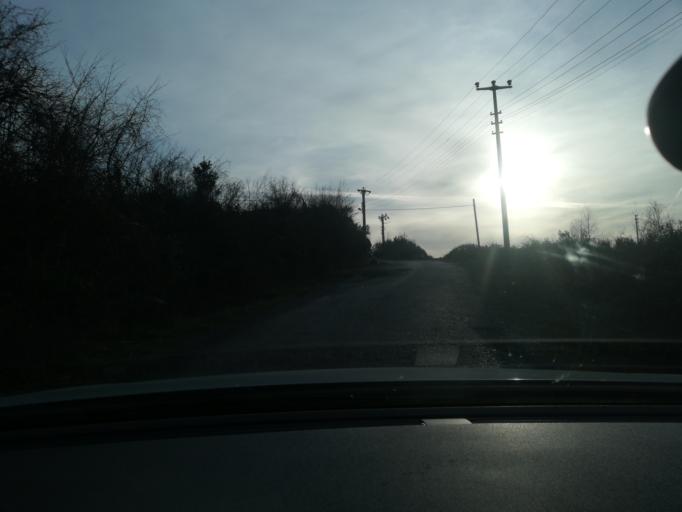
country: TR
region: Zonguldak
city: Tieum
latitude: 41.5569
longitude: 32.0272
